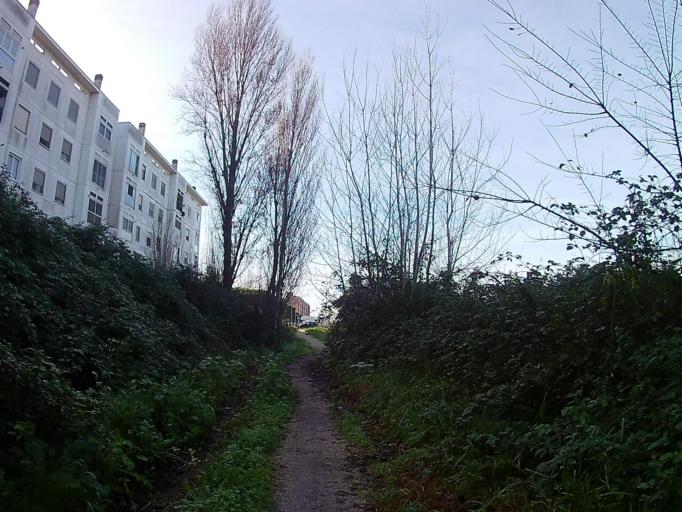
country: IT
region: Latium
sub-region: Citta metropolitana di Roma Capitale
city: Lido di Ostia
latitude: 41.7432
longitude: 12.2640
